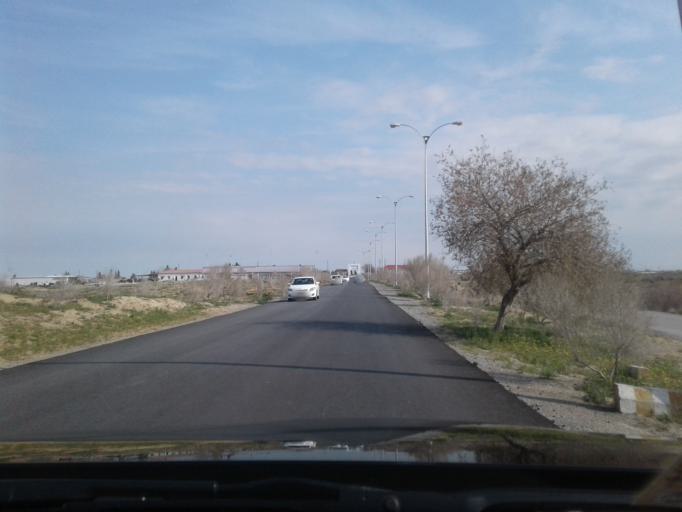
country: TM
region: Ahal
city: Ashgabat
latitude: 38.0941
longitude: 58.3841
